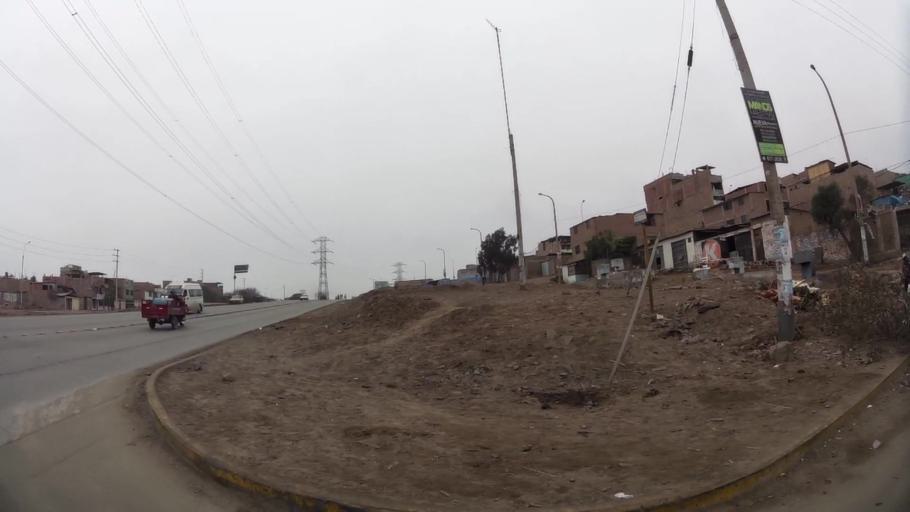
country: PE
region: Lima
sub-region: Lima
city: Surco
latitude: -12.2267
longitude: -76.9163
